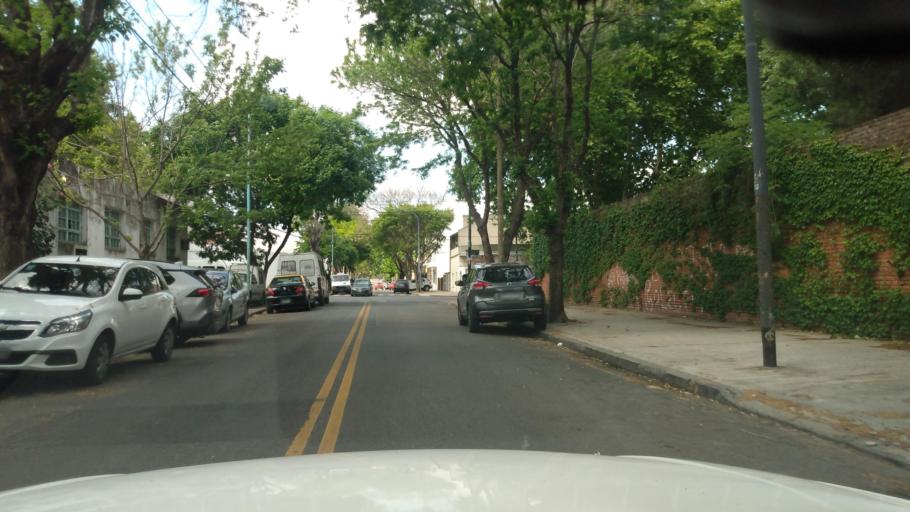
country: AR
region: Buenos Aires
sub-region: Partido de General San Martin
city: General San Martin
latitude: -34.5781
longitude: -58.5117
